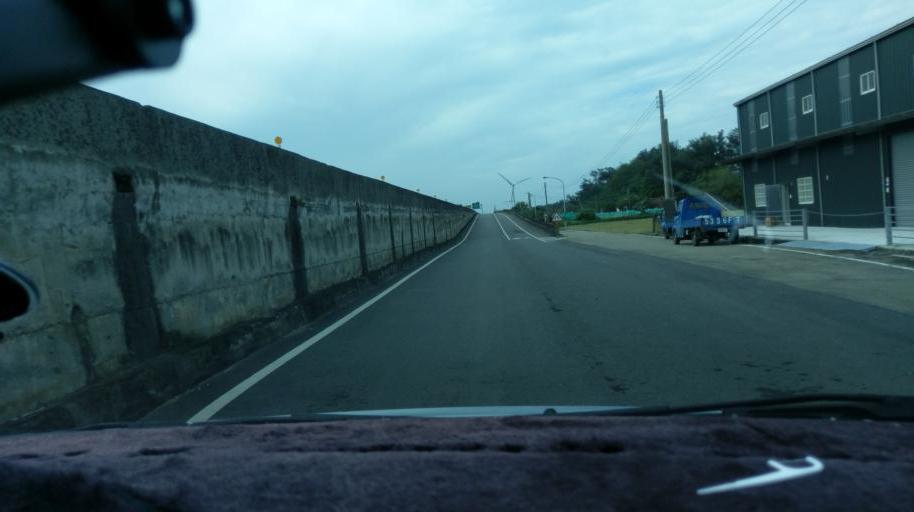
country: TW
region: Taiwan
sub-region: Hsinchu
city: Hsinchu
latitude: 24.7320
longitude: 120.8788
